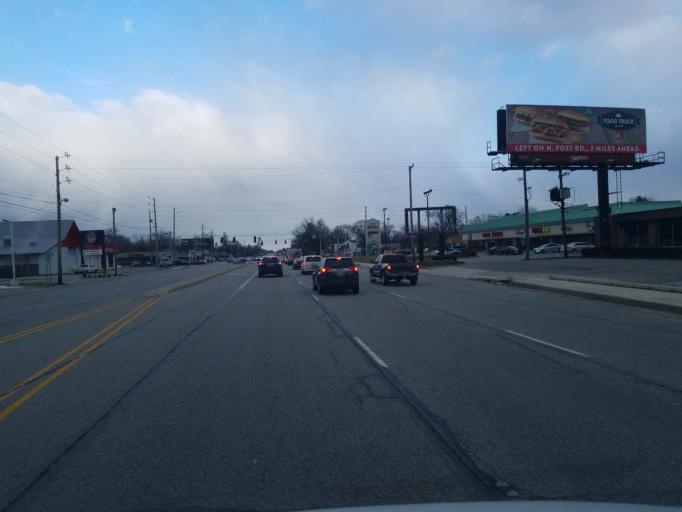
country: US
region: Indiana
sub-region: Marion County
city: Warren Park
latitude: 39.7738
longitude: -86.0111
